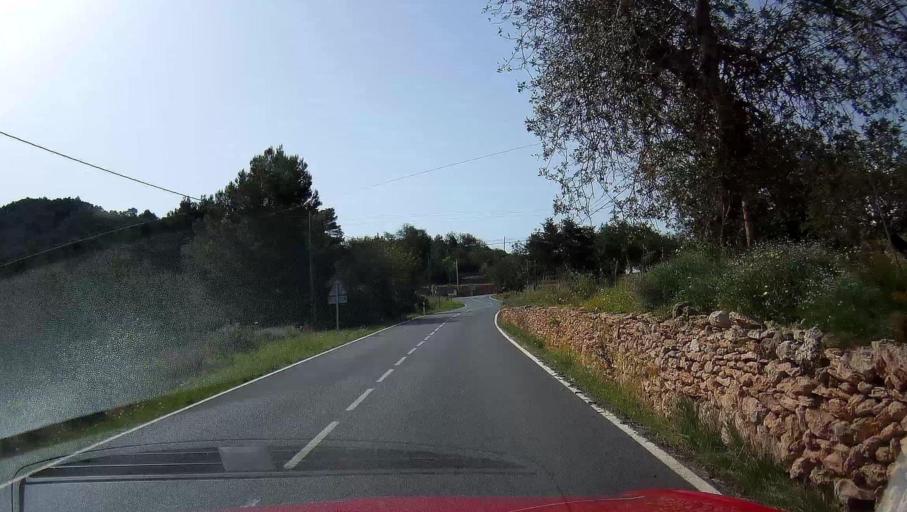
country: ES
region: Balearic Islands
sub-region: Illes Balears
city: Santa Eularia des Riu
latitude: 39.0403
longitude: 1.5660
